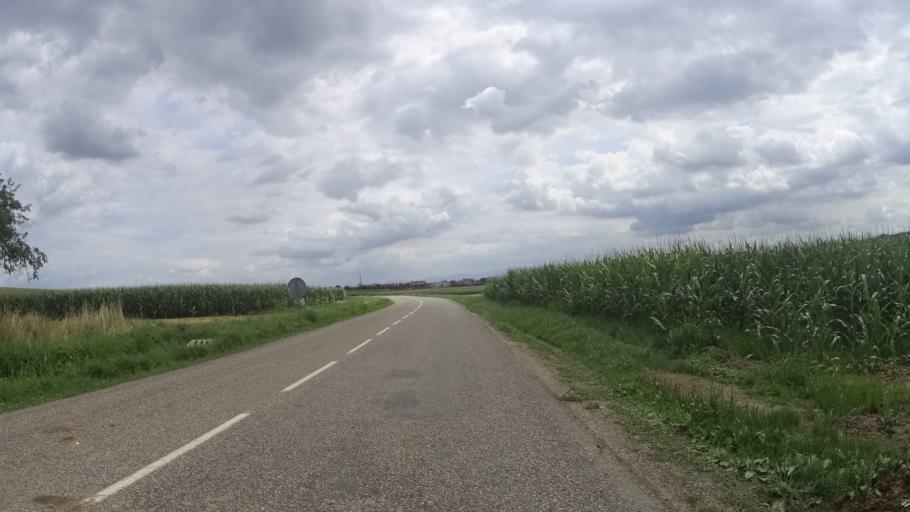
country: FR
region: Alsace
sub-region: Departement du Bas-Rhin
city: Geudertheim
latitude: 48.7213
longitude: 7.7666
